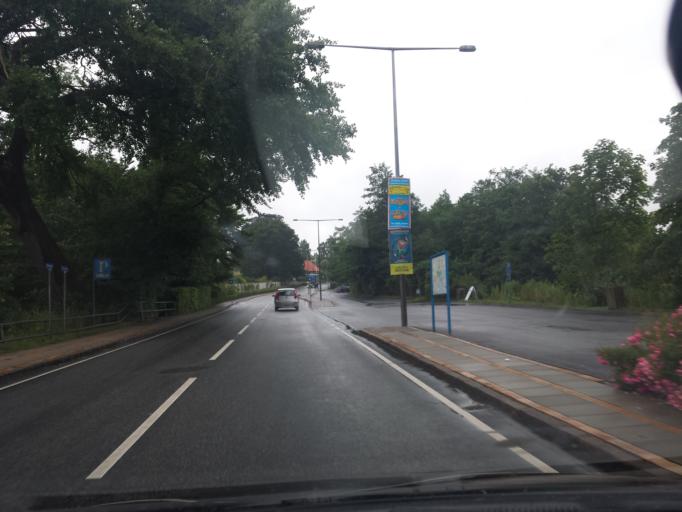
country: DK
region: South Denmark
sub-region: Sonderborg Kommune
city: Grasten
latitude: 54.9238
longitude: 9.5965
